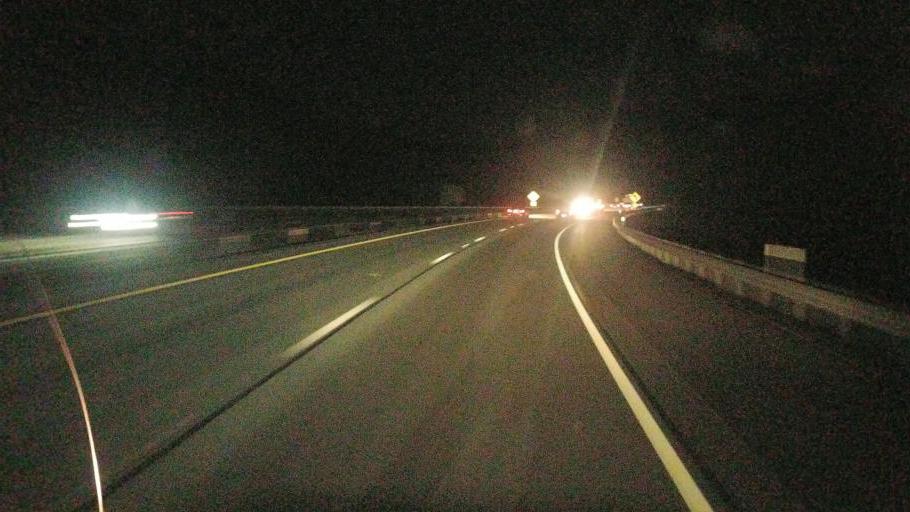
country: US
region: West Virginia
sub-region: Mercer County
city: Princeton
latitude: 37.3476
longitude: -81.0561
